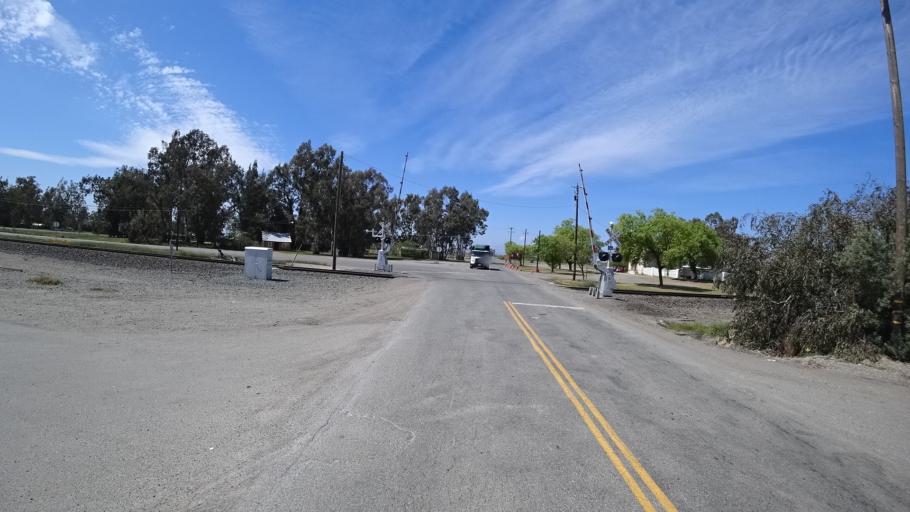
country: US
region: California
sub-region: Glenn County
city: Willows
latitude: 39.6241
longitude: -122.1937
